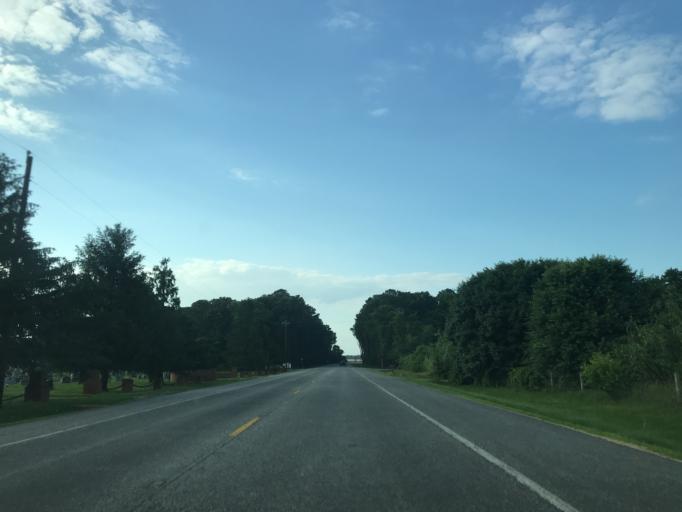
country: US
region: Maryland
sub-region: Caroline County
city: Denton
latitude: 38.8002
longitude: -75.7868
